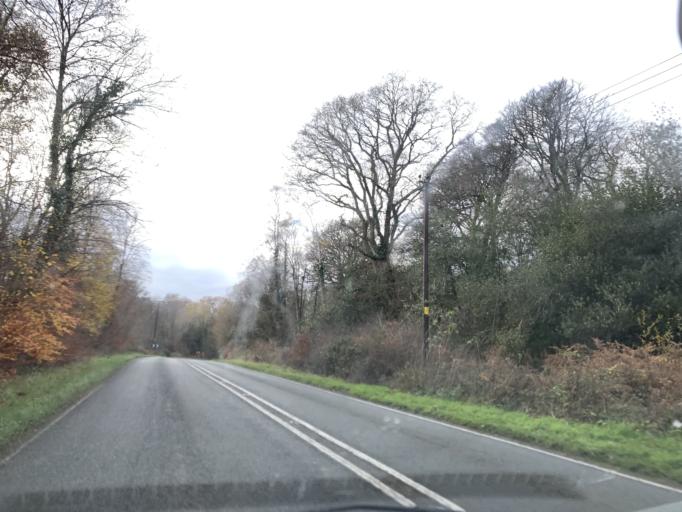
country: GB
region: England
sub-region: Hampshire
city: Lyndhurst
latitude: 50.8598
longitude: -1.6035
